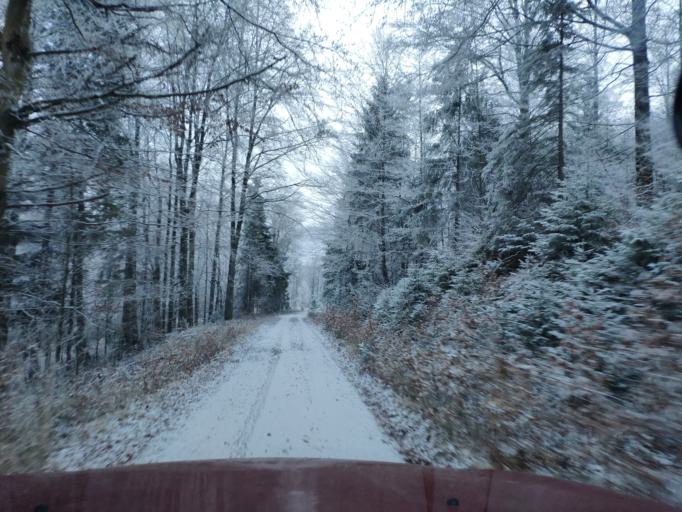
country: SK
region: Kosicky
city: Dobsina
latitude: 48.8116
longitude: 20.4935
